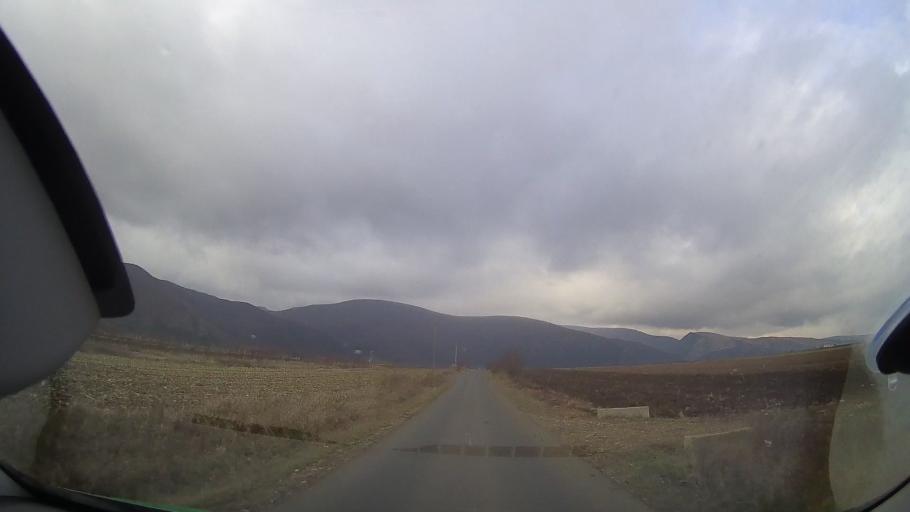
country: RO
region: Cluj
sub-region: Comuna Moldovenesti
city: Moldovenesti
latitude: 46.5054
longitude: 23.6745
